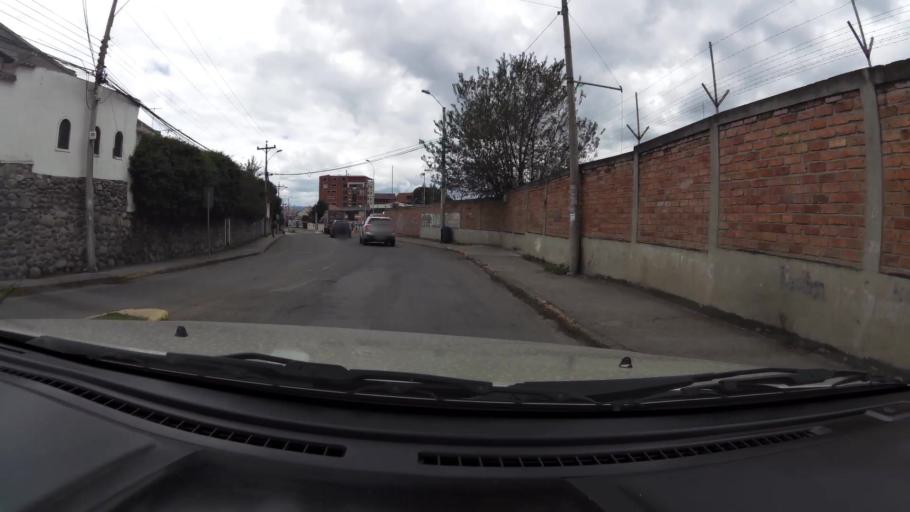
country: EC
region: Azuay
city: Cuenca
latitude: -2.8892
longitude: -79.0242
